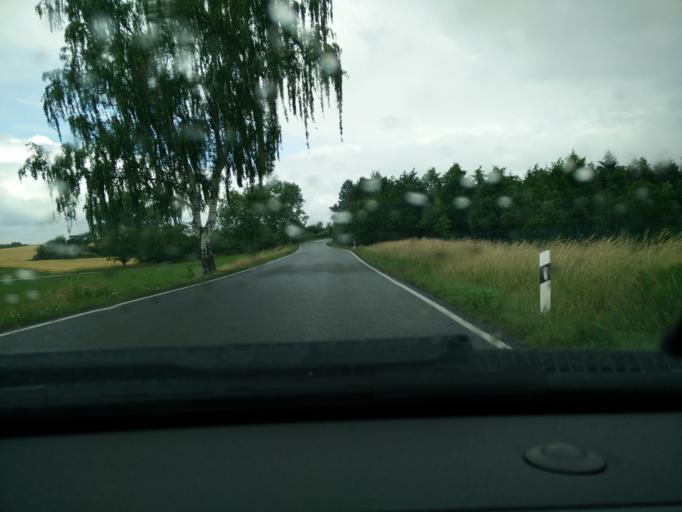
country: DE
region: Saxony
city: Grossbardau
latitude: 51.2110
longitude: 12.7037
